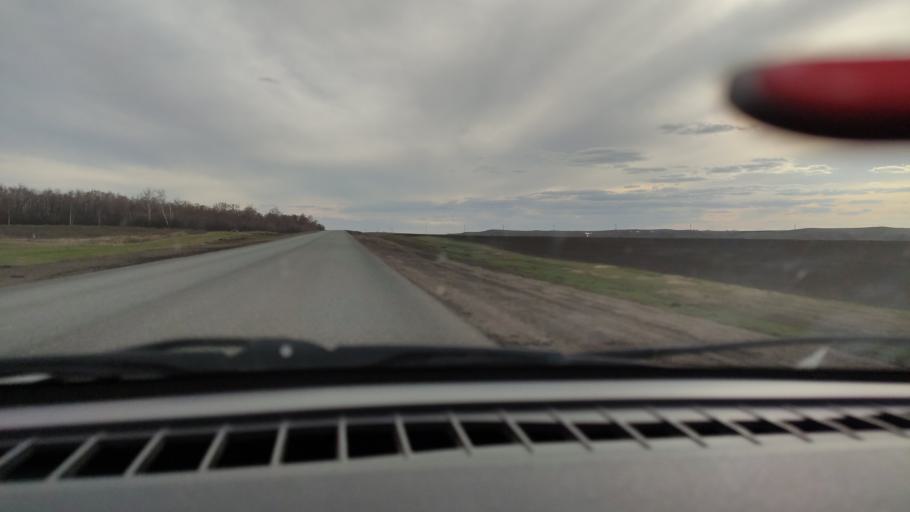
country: RU
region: Bashkortostan
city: Yermolayevo
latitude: 52.4633
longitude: 55.8261
